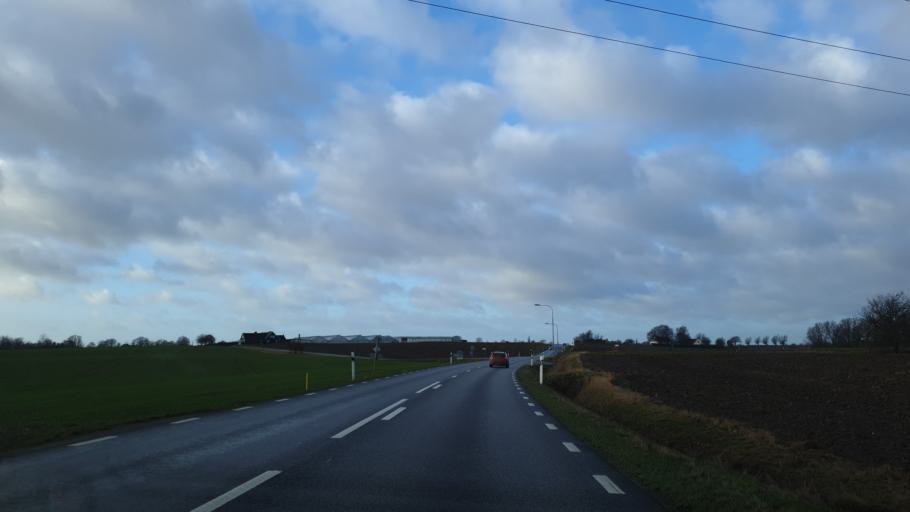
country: SE
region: Skane
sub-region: Trelleborgs Kommun
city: Trelleborg
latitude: 55.4555
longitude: 13.1723
